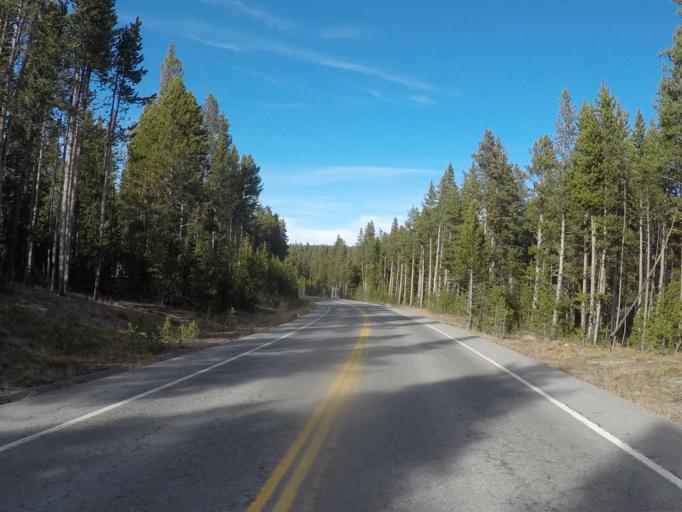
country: US
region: Montana
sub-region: Gallatin County
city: West Yellowstone
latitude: 44.7317
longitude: -110.6957
